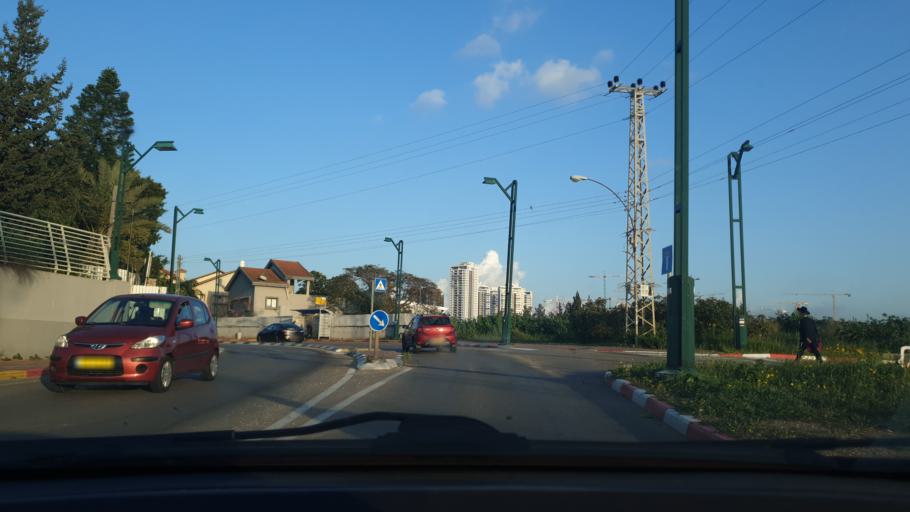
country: IL
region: Central District
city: Ramla
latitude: 31.9354
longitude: 34.8404
